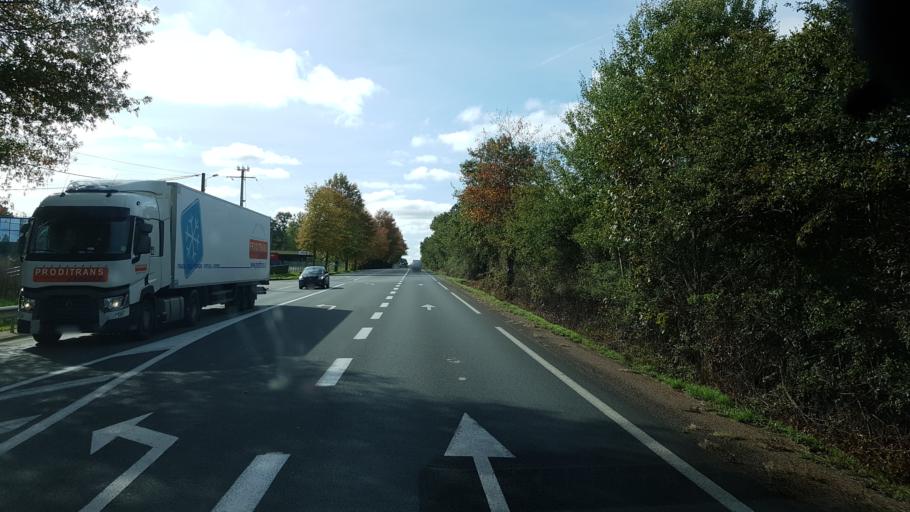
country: FR
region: Limousin
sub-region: Departement de la Haute-Vienne
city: Bellac
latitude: 46.1331
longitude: 1.0884
